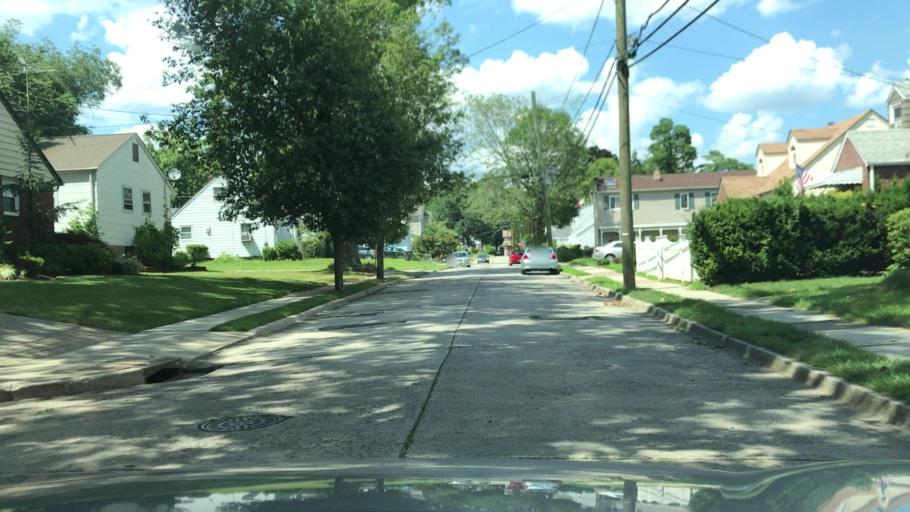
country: US
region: New Jersey
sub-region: Bergen County
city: Bergenfield
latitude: 40.9218
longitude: -74.0047
